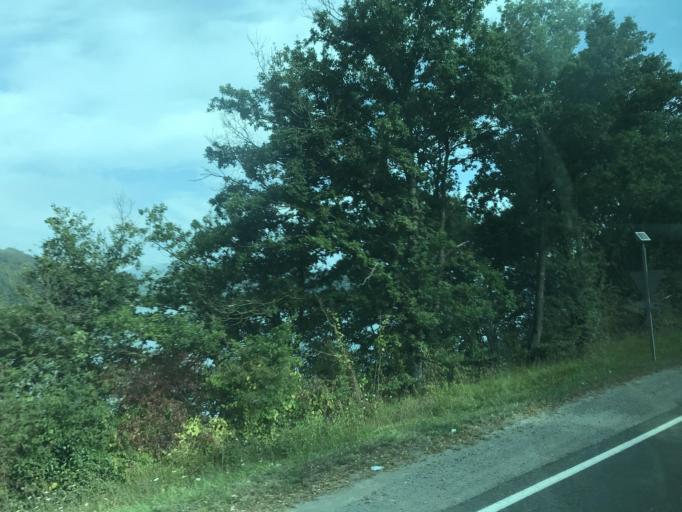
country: ES
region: Basque Country
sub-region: Bizkaia
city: Otxandio
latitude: 42.9836
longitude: -2.6452
